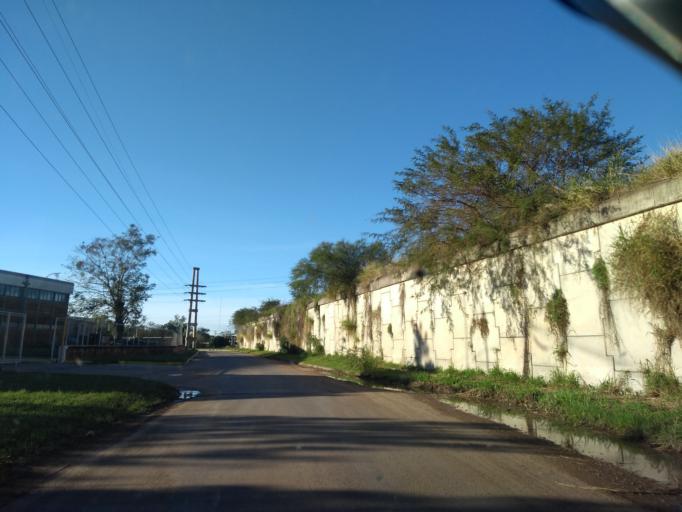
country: AR
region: Chaco
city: Barranqueras
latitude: -27.4921
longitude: -58.9278
